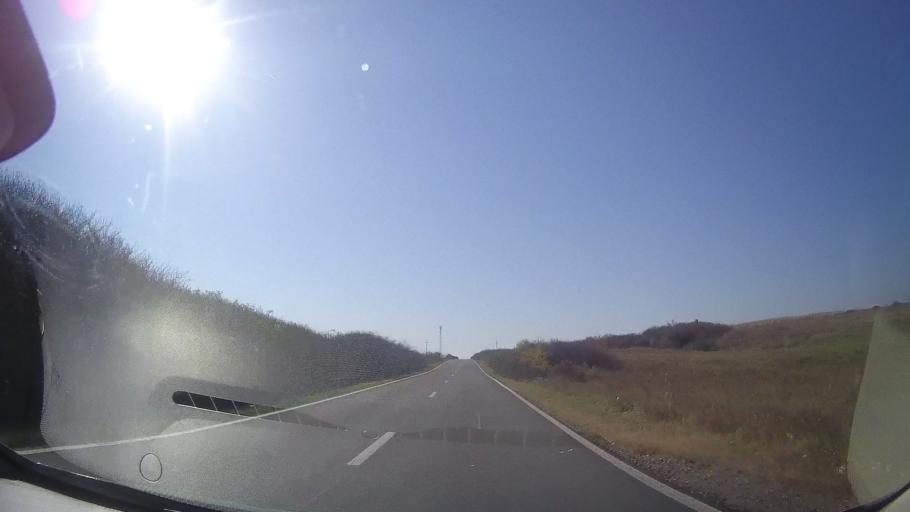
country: RO
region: Timis
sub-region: Comuna Belint
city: Belint
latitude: 45.7695
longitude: 21.7293
